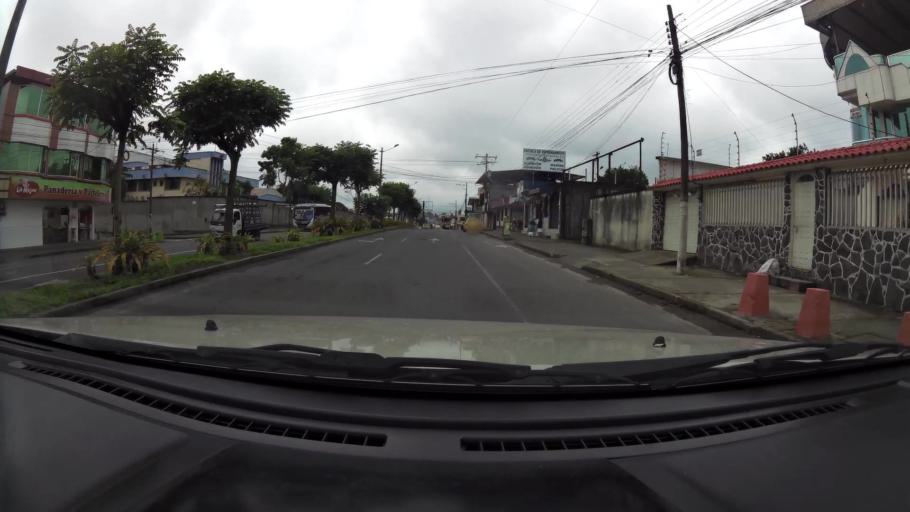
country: EC
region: Santo Domingo de los Tsachilas
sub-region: Canton Santo Domingo de los Colorados
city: Santo Domingo de los Colorados
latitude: -0.2578
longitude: -79.1611
